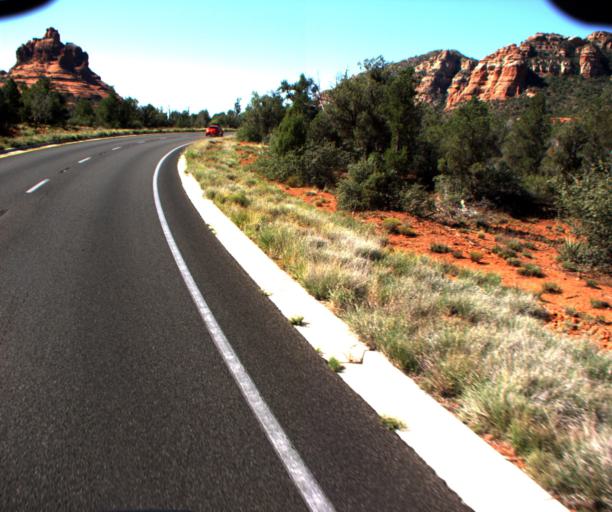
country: US
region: Arizona
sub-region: Yavapai County
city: Village of Oak Creek (Big Park)
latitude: 34.8102
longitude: -111.7679
